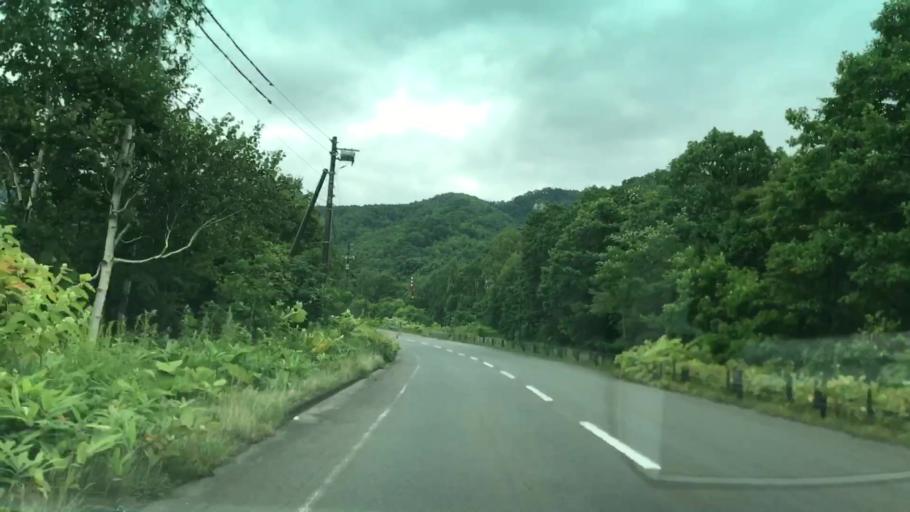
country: JP
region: Hokkaido
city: Yoichi
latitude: 43.0121
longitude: 140.8686
